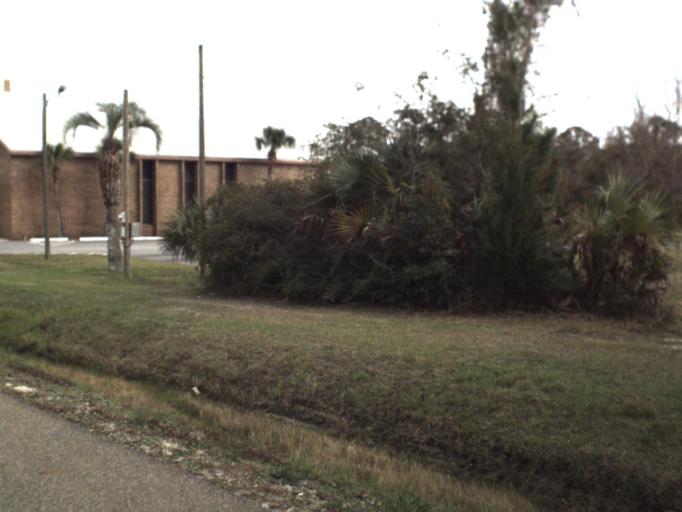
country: US
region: Florida
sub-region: Bay County
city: Callaway
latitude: 30.1529
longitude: -85.5713
